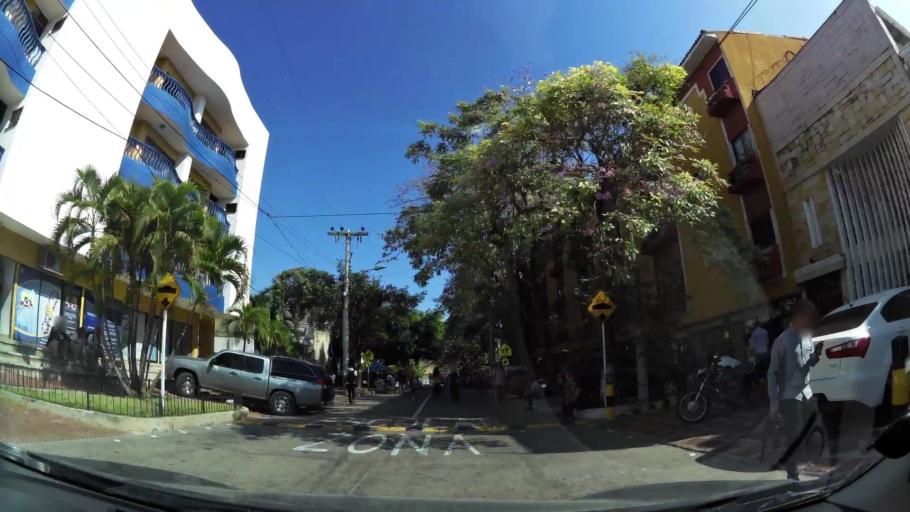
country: CO
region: Atlantico
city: Barranquilla
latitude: 10.9902
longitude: -74.7935
